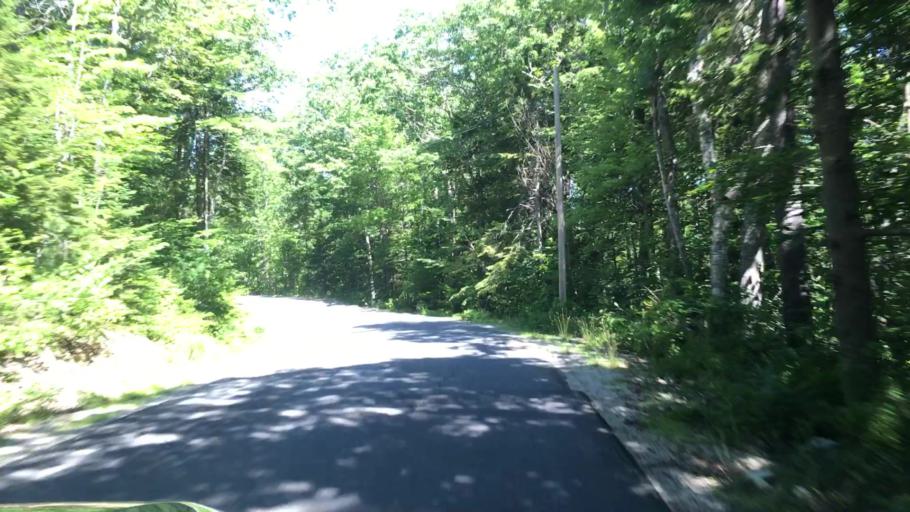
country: US
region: Maine
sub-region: Hancock County
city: Sedgwick
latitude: 44.3366
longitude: -68.6622
